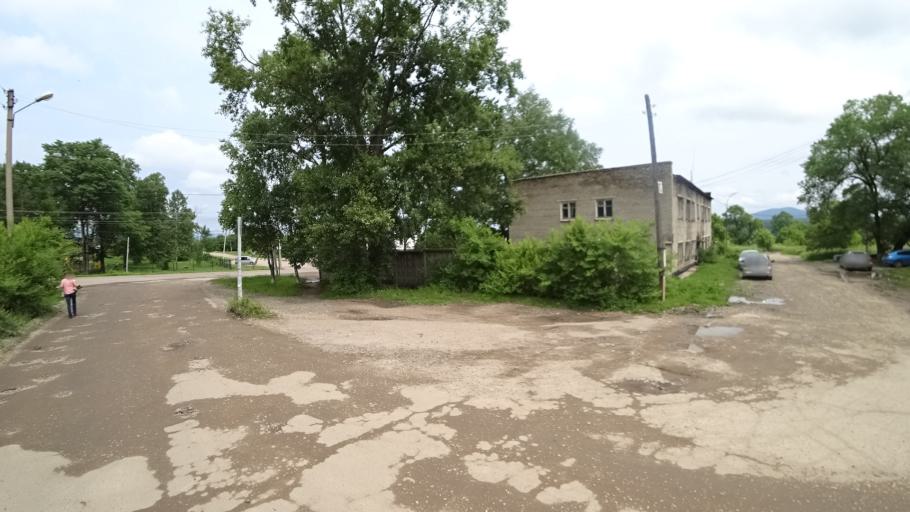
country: RU
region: Primorskiy
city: Novosysoyevka
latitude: 44.2288
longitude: 133.3609
